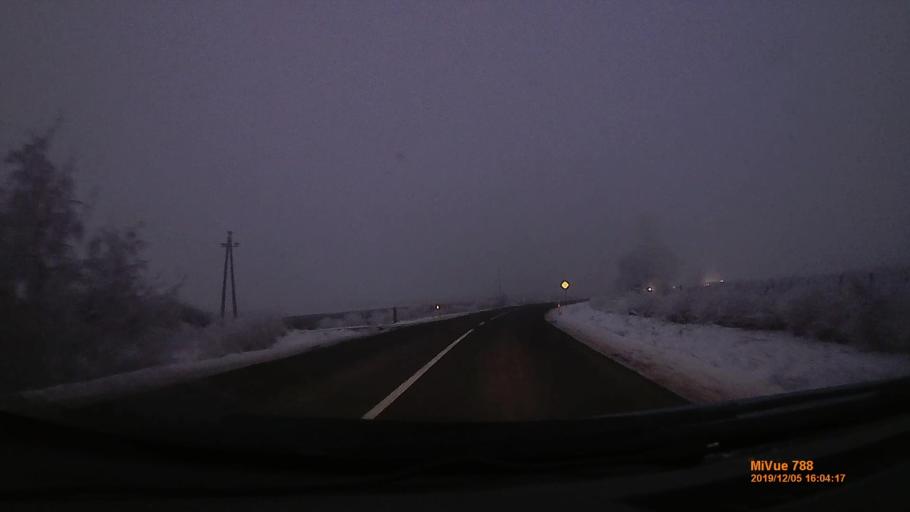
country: HU
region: Borsod-Abauj-Zemplen
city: Tarcal
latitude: 48.1063
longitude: 21.3550
